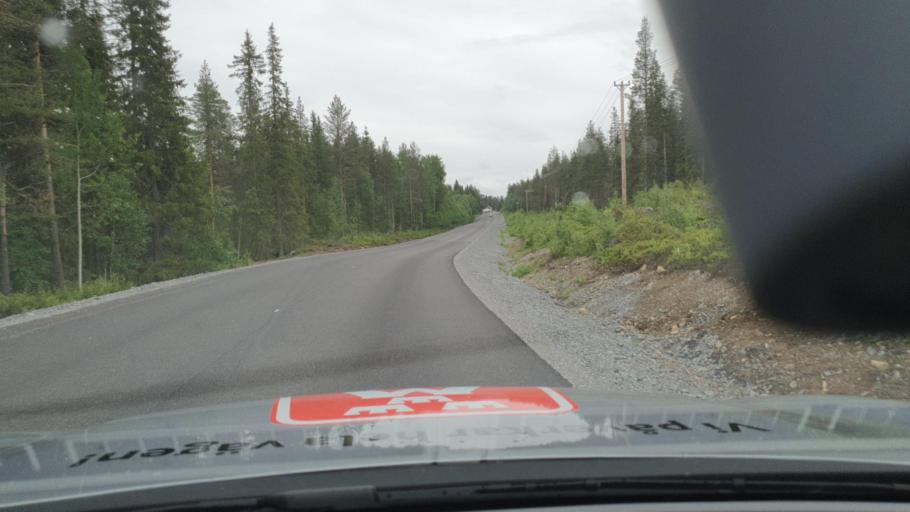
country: SE
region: Norrbotten
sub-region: Overtornea Kommun
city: OEvertornea
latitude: 66.6233
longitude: 23.2842
